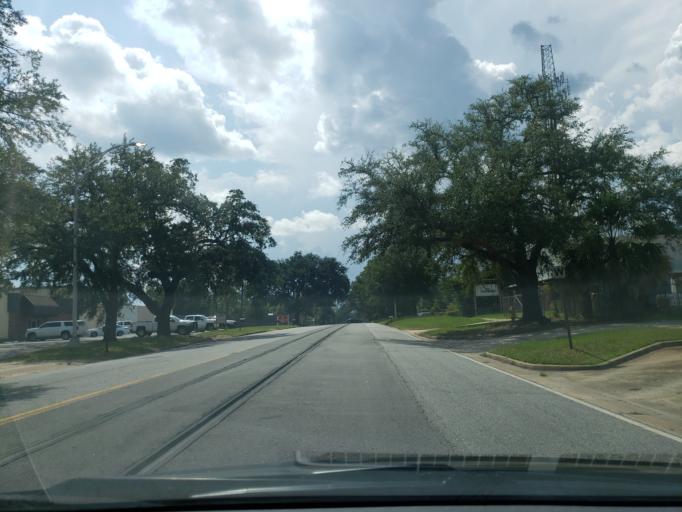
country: US
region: Georgia
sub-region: Dougherty County
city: Albany
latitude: 31.5816
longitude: -84.1573
